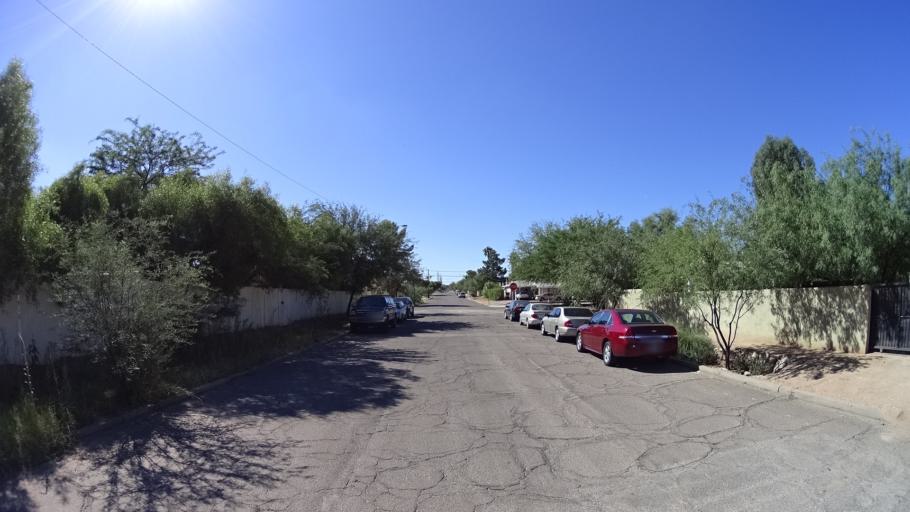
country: US
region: Arizona
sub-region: Pima County
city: Tucson
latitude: 32.2472
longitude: -110.9498
